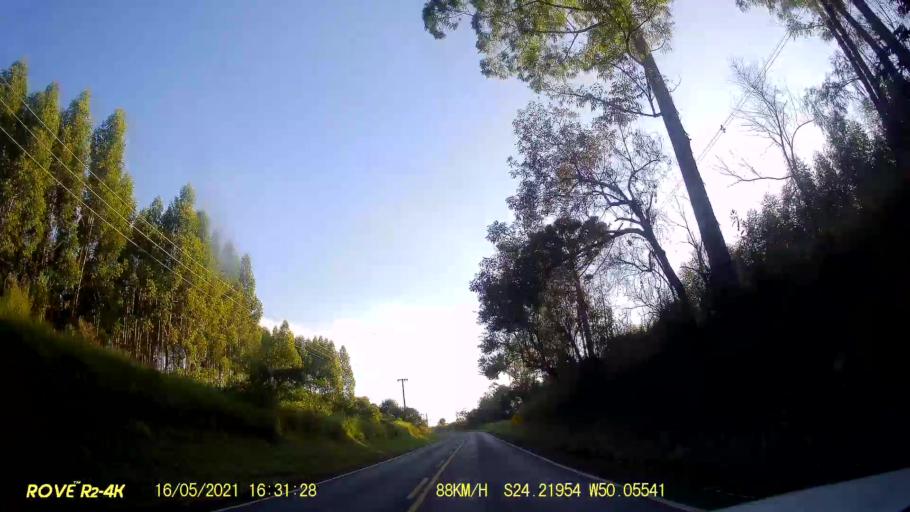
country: BR
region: Parana
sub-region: Pirai Do Sul
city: Pirai do Sul
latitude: -24.2196
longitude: -50.0554
